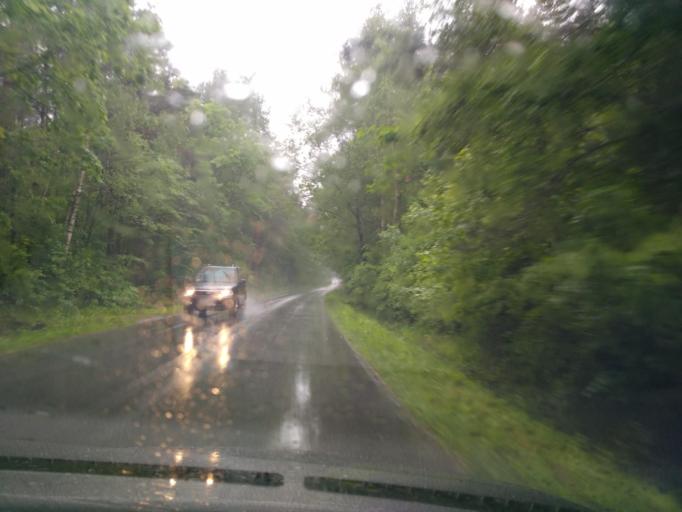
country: PL
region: Subcarpathian Voivodeship
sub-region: Powiat jasielski
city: Debowiec
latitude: 49.6628
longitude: 21.4361
